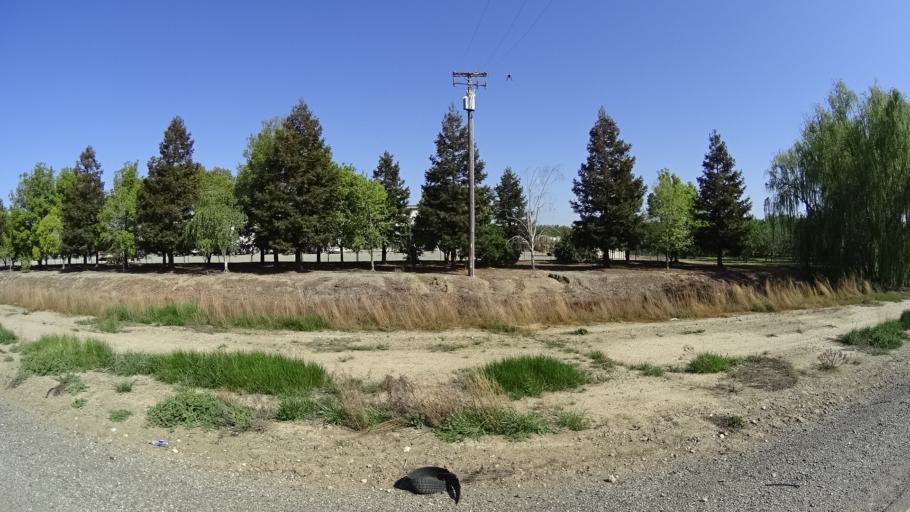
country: US
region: California
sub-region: Glenn County
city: Hamilton City
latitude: 39.6597
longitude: -122.0354
